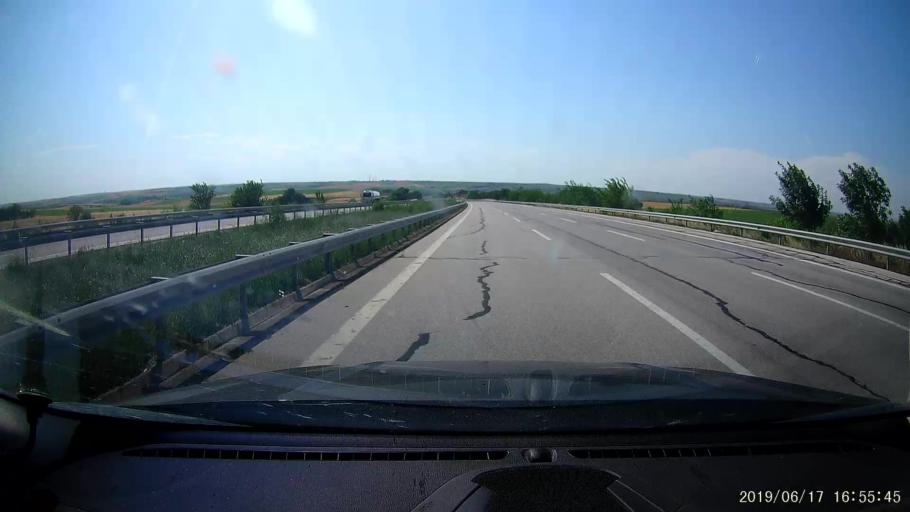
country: TR
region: Edirne
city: Haskoy
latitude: 41.5812
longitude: 26.9564
